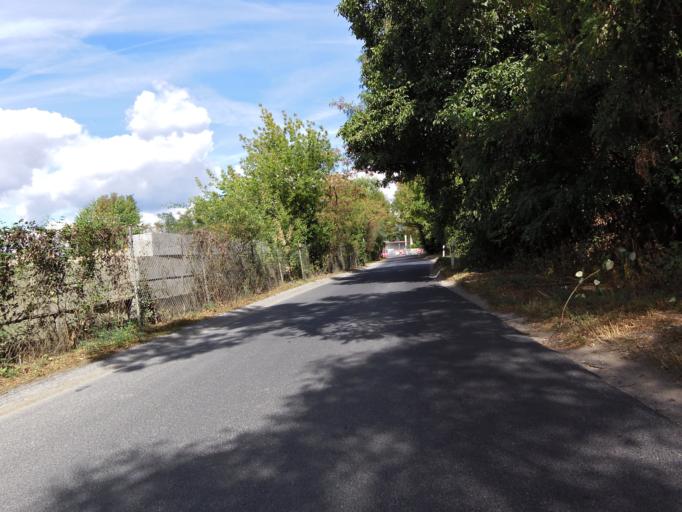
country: DE
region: Bavaria
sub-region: Regierungsbezirk Unterfranken
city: Zell am Main
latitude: 49.8200
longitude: 9.8753
